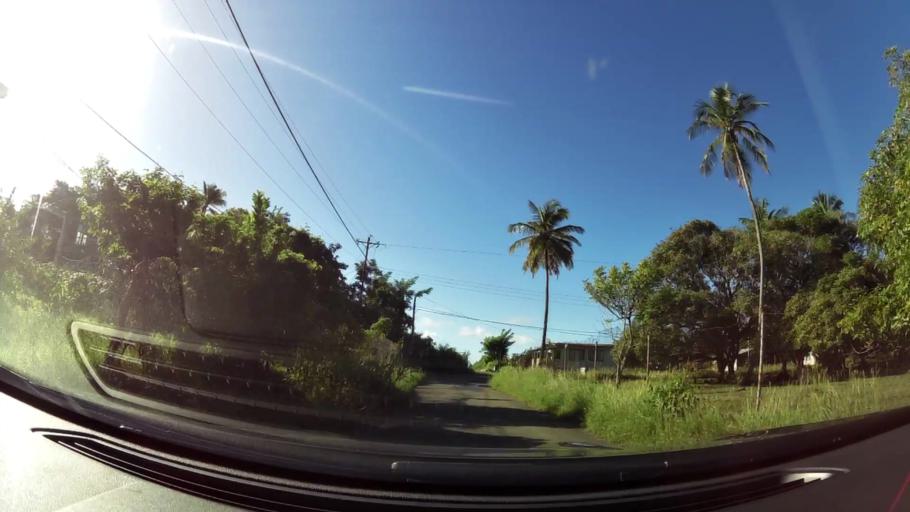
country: TT
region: Tobago
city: Scarborough
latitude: 11.1514
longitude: -60.8264
